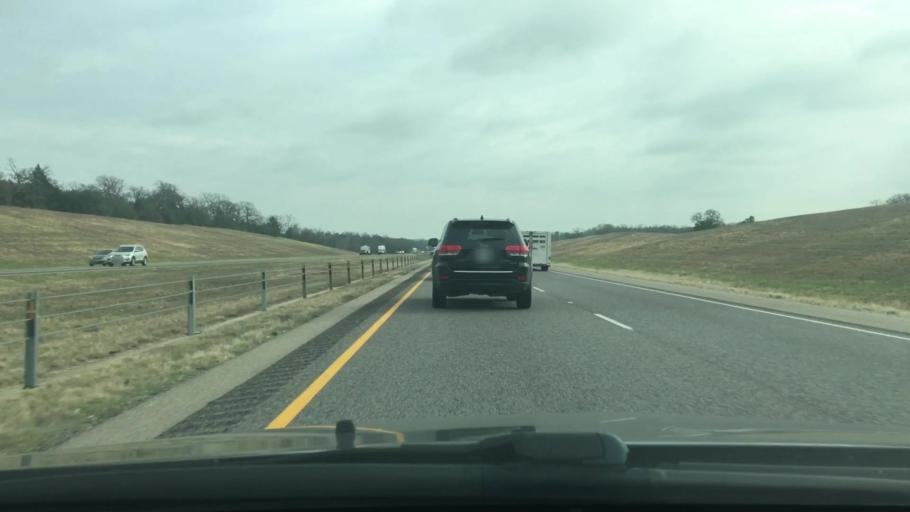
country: US
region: Texas
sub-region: Leon County
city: Buffalo
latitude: 31.5161
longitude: -96.1069
